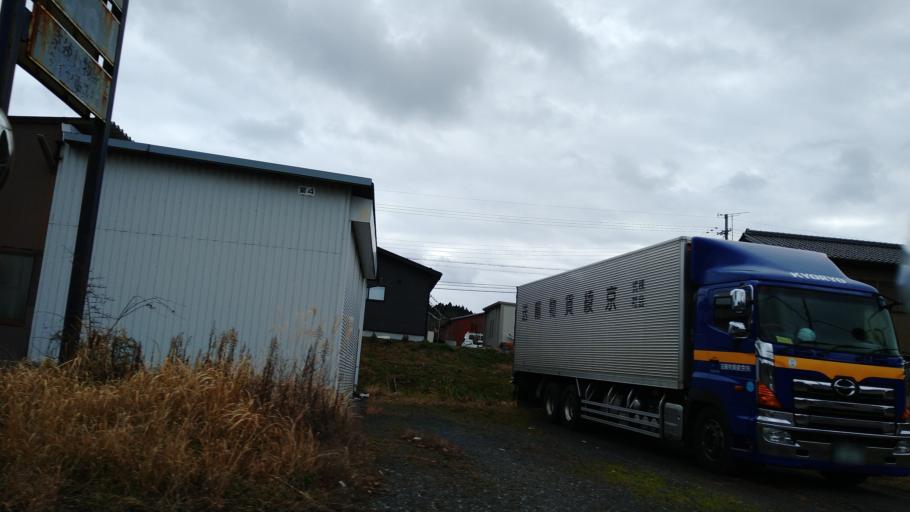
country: JP
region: Kyoto
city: Maizuru
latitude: 35.3619
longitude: 135.3187
